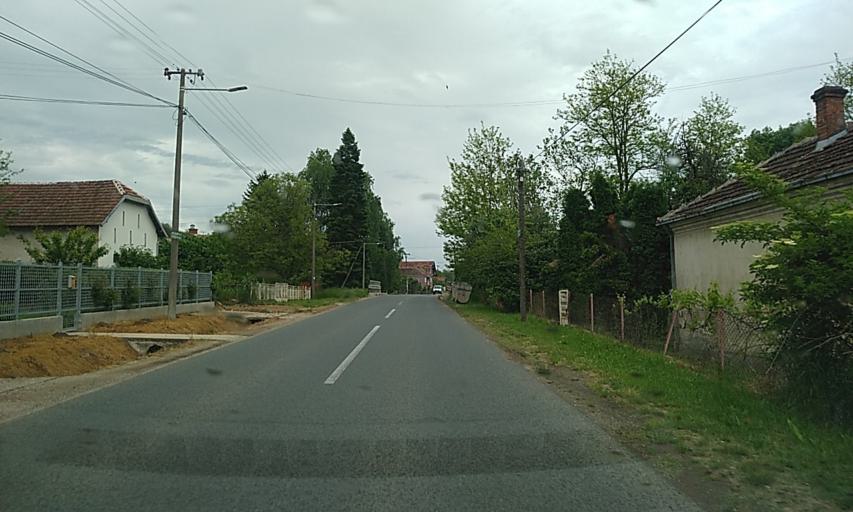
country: RS
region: Central Serbia
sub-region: Rasinski Okrug
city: Krusevac
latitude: 43.5717
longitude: 21.4162
